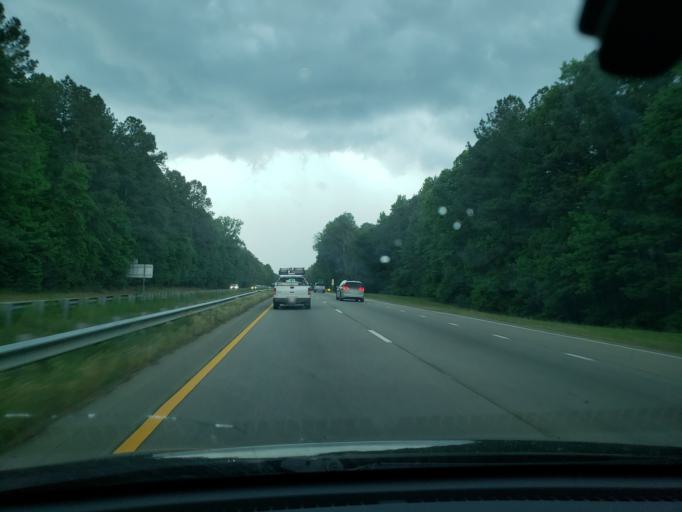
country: US
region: North Carolina
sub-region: Durham County
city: Durham
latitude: 35.9865
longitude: -78.9580
